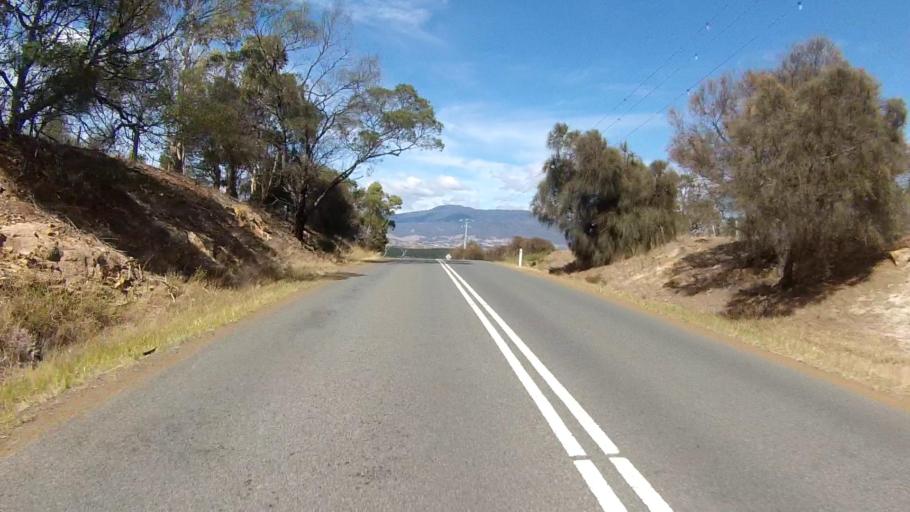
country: AU
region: Tasmania
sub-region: Brighton
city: Bridgewater
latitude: -42.7071
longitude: 147.2700
